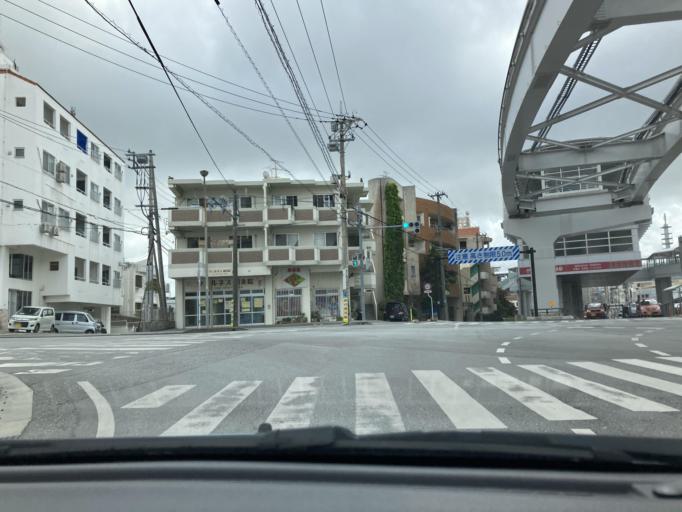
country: JP
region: Okinawa
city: Ginowan
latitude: 26.2280
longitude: 127.7292
